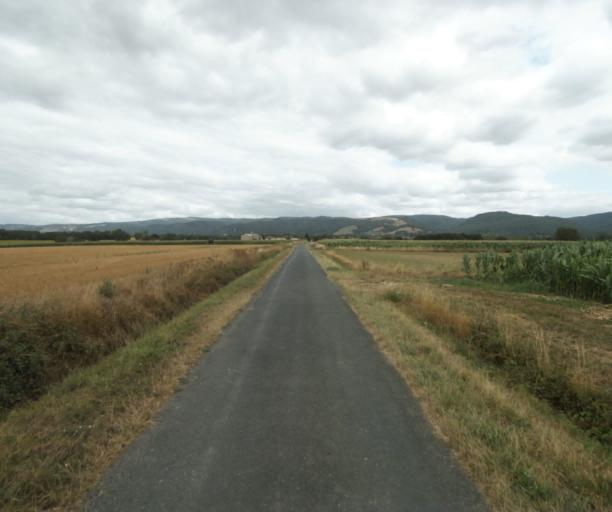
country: FR
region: Midi-Pyrenees
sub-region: Departement du Tarn
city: Soreze
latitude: 43.4735
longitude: 2.0516
